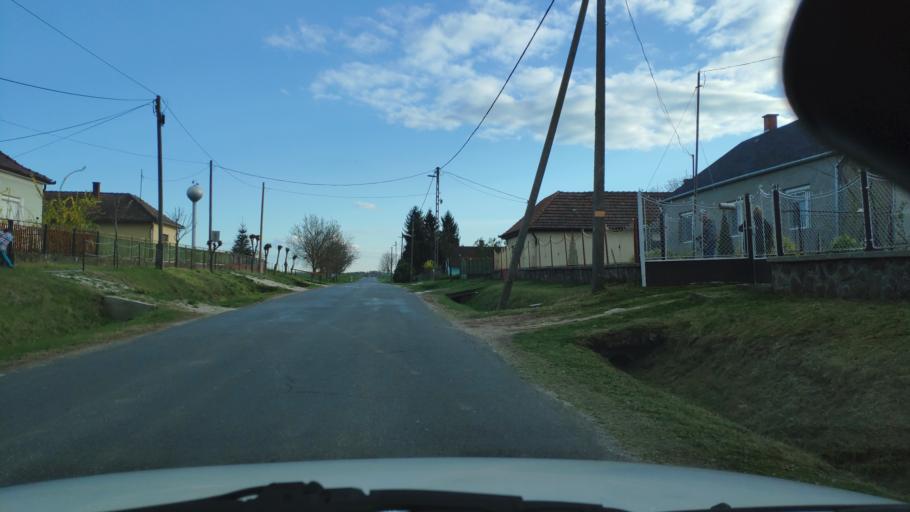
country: HU
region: Zala
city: Zalakomar
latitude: 46.4801
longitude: 17.1282
